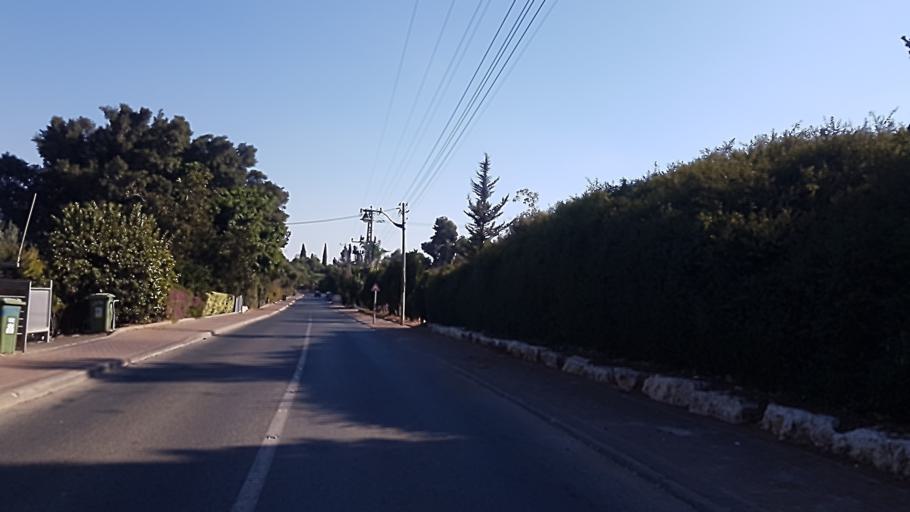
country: IL
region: Central District
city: Kfar Saba
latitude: 32.2068
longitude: 34.9041
